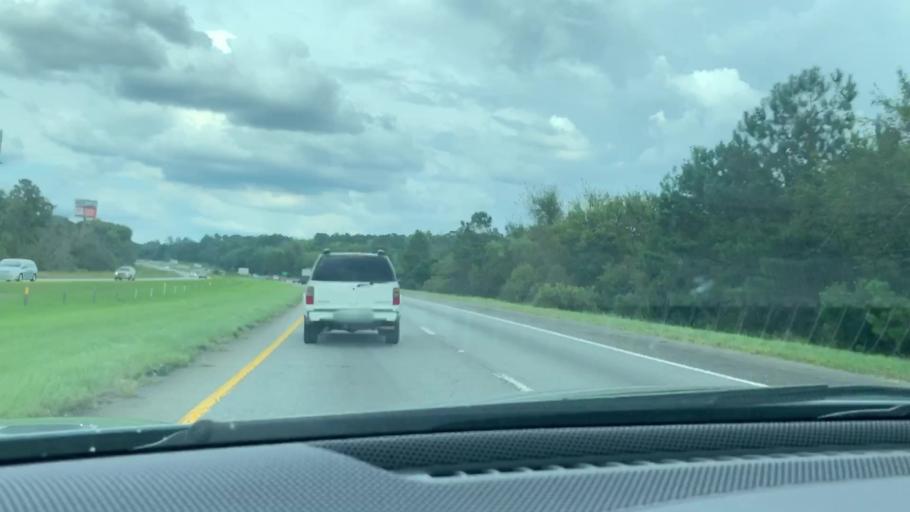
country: US
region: South Carolina
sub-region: Hampton County
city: Yemassee
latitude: 32.5980
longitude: -80.9059
